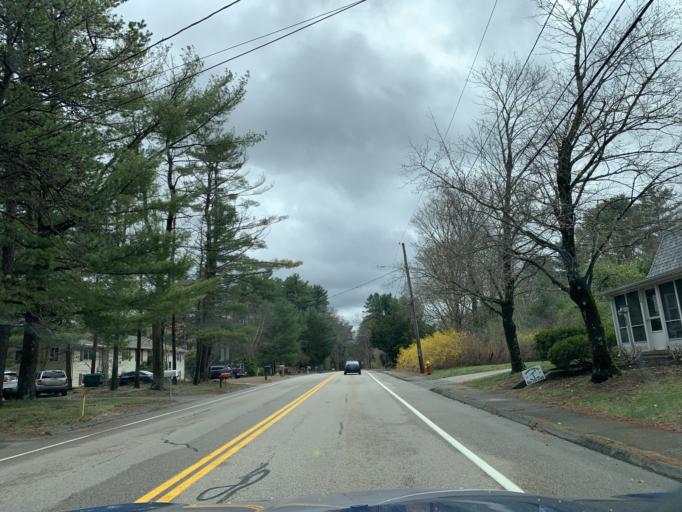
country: US
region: Massachusetts
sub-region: Bristol County
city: Mansfield Center
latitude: 41.9816
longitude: -71.2430
